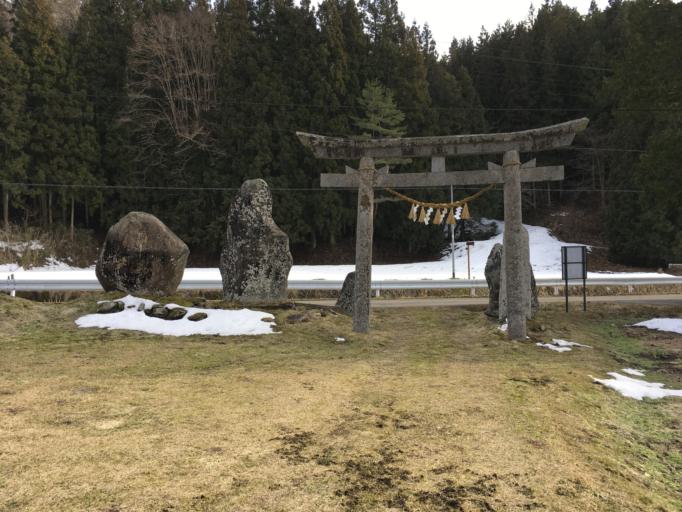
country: JP
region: Iwate
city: Tono
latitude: 39.2372
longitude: 141.3382
